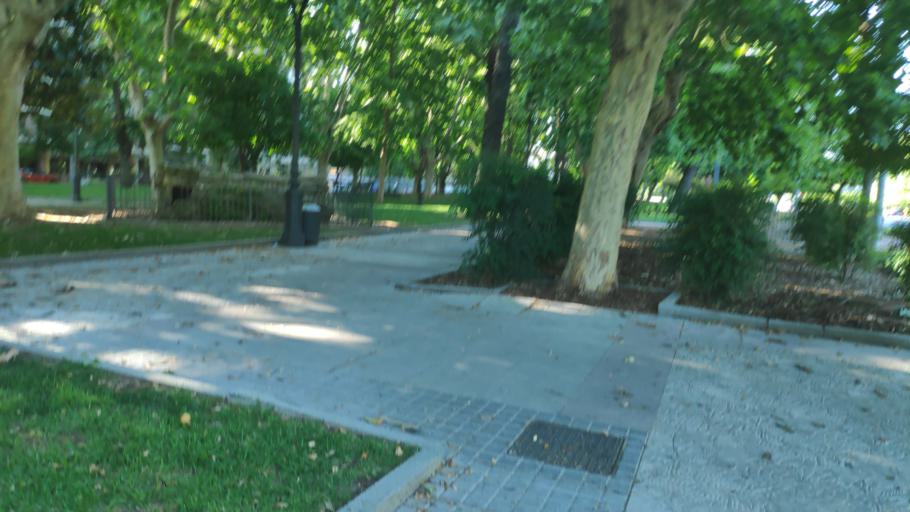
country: ES
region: Andalusia
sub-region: Province of Cordoba
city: Cordoba
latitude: 37.8764
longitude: -4.7864
